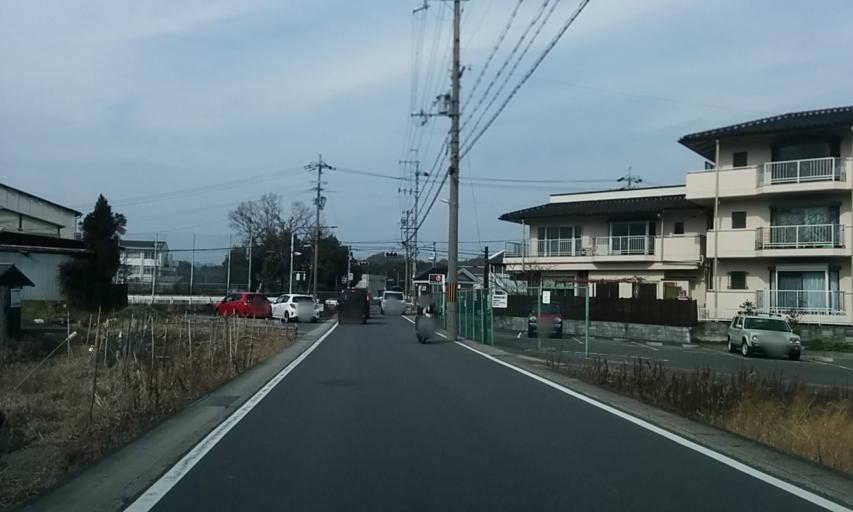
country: JP
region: Kyoto
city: Muko
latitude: 34.9505
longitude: 135.6857
